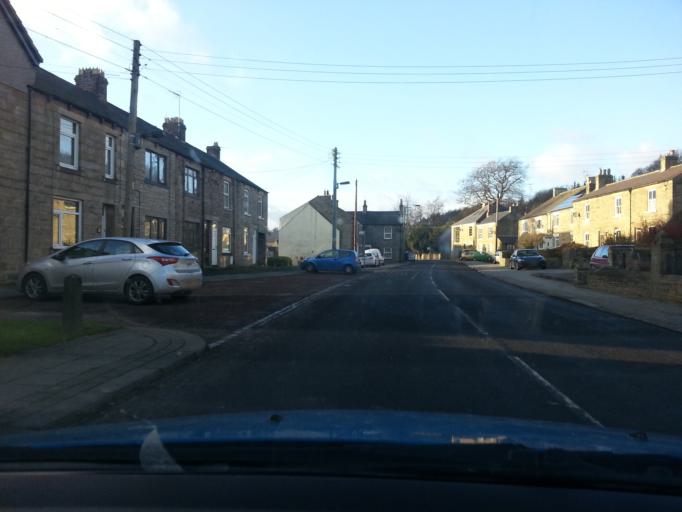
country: GB
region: England
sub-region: County Durham
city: Stanhope
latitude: 54.7273
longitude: -1.9567
